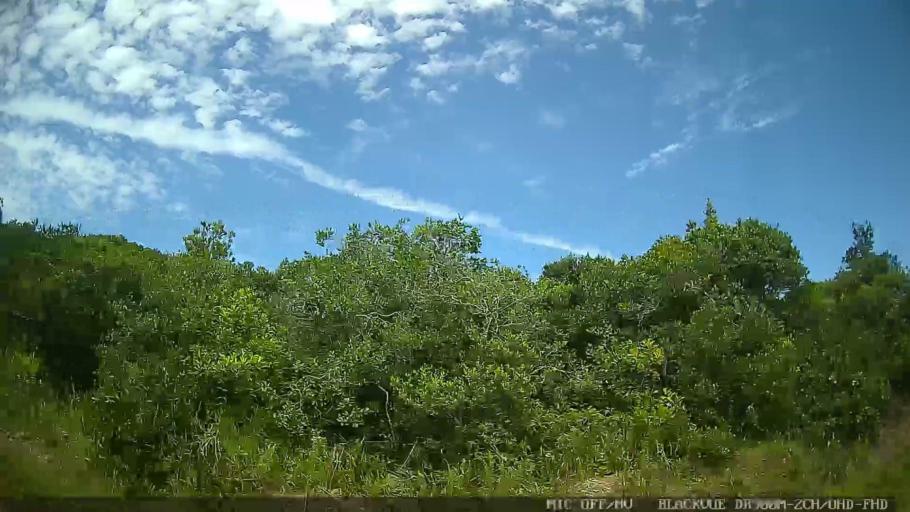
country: BR
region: Sao Paulo
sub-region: Iguape
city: Iguape
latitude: -24.7155
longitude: -47.5148
